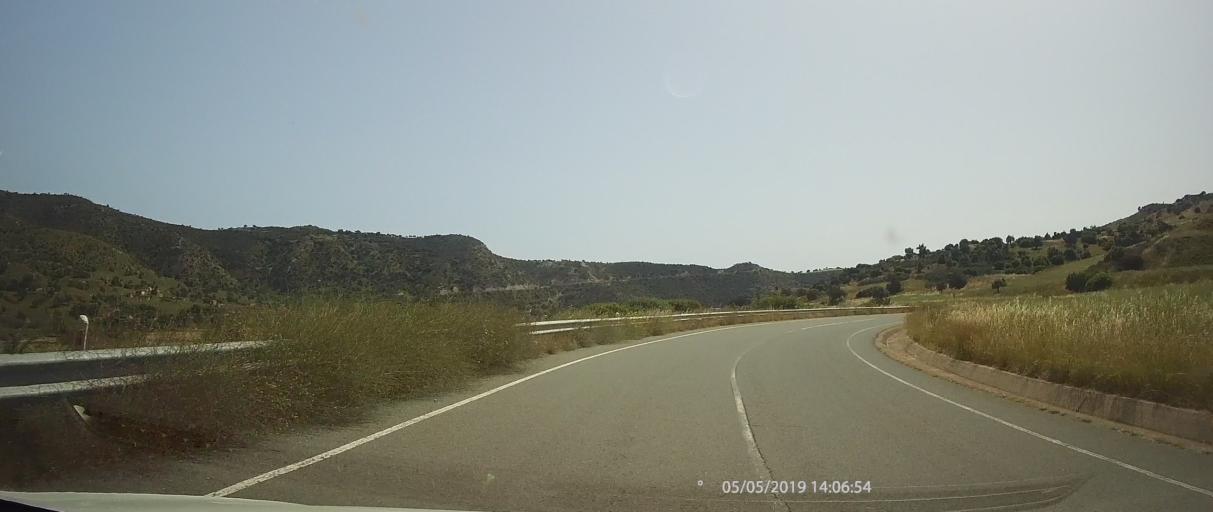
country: CY
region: Limassol
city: Pissouri
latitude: 34.7404
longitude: 32.6029
